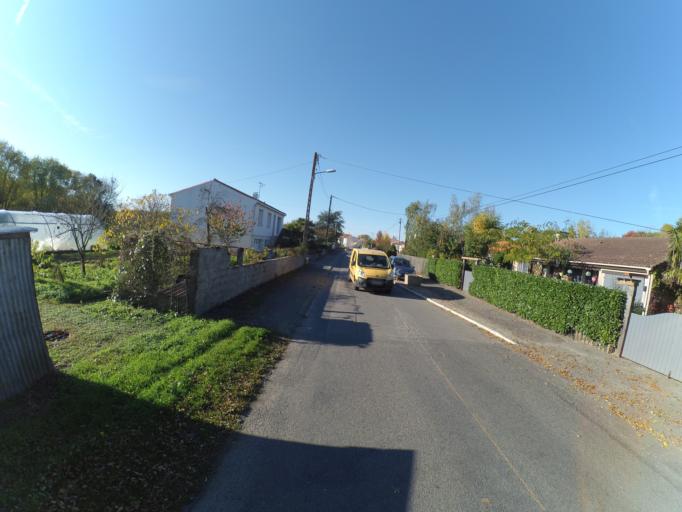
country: FR
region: Pays de la Loire
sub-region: Departement de la Loire-Atlantique
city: Saint-Lumine-de-Clisson
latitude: 47.0817
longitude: -1.3330
